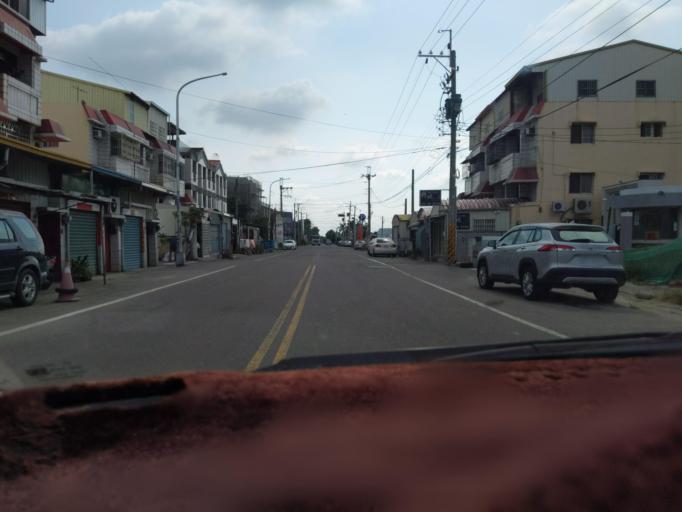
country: TW
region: Taiwan
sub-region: Yunlin
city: Douliu
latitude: 23.8026
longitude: 120.4513
